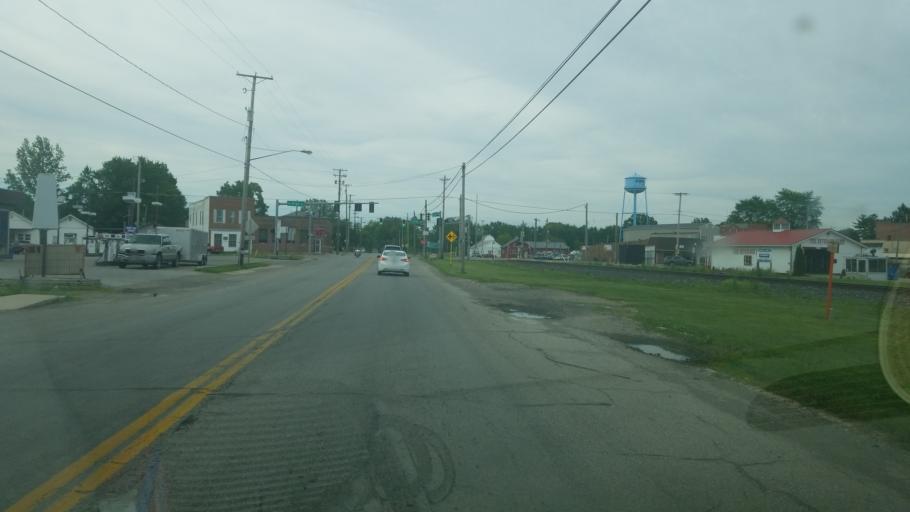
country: US
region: Ohio
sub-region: Delaware County
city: Ashley
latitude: 40.4082
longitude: -82.9562
